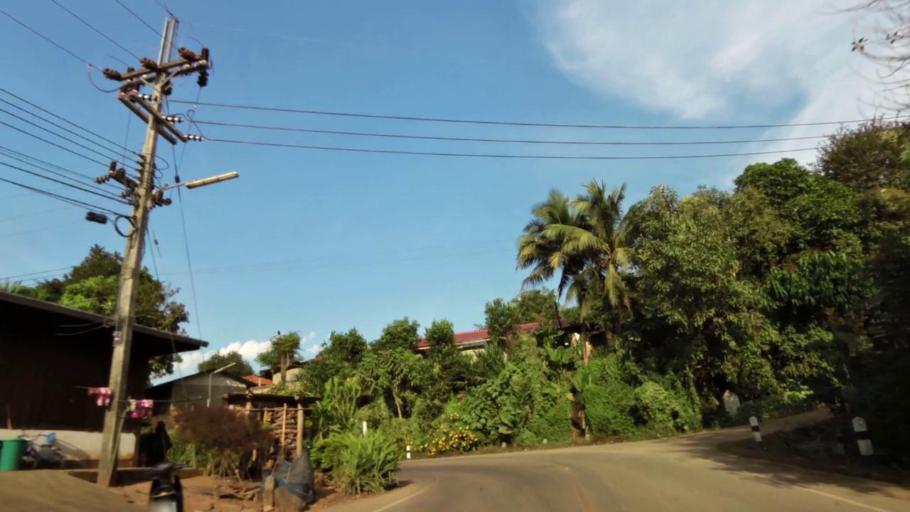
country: TH
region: Chiang Rai
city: Khun Tan
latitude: 19.8673
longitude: 100.3993
